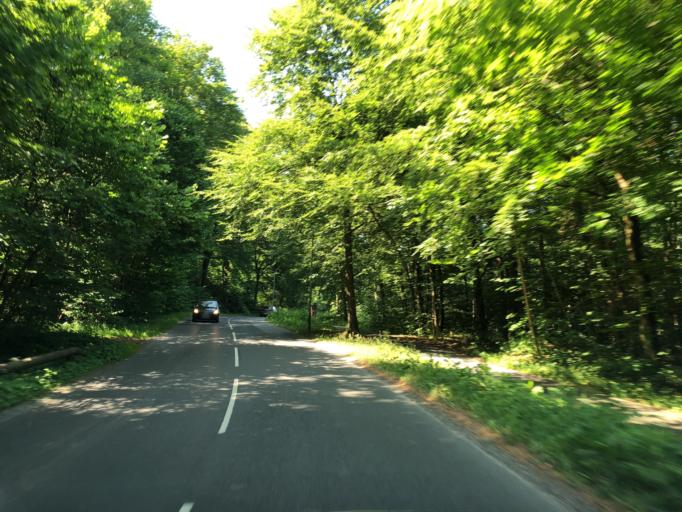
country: DK
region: South Denmark
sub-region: Kolding Kommune
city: Kolding
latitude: 55.5141
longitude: 9.4892
